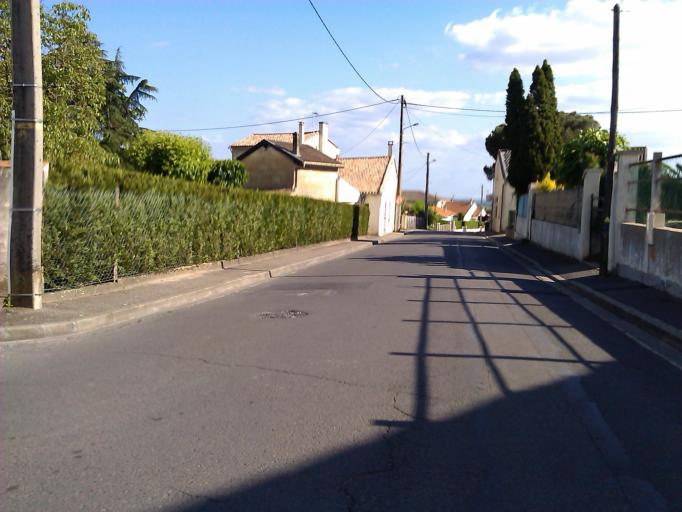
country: FR
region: Aquitaine
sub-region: Departement de la Gironde
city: Saint-Gervais
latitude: 44.9970
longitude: -0.4486
